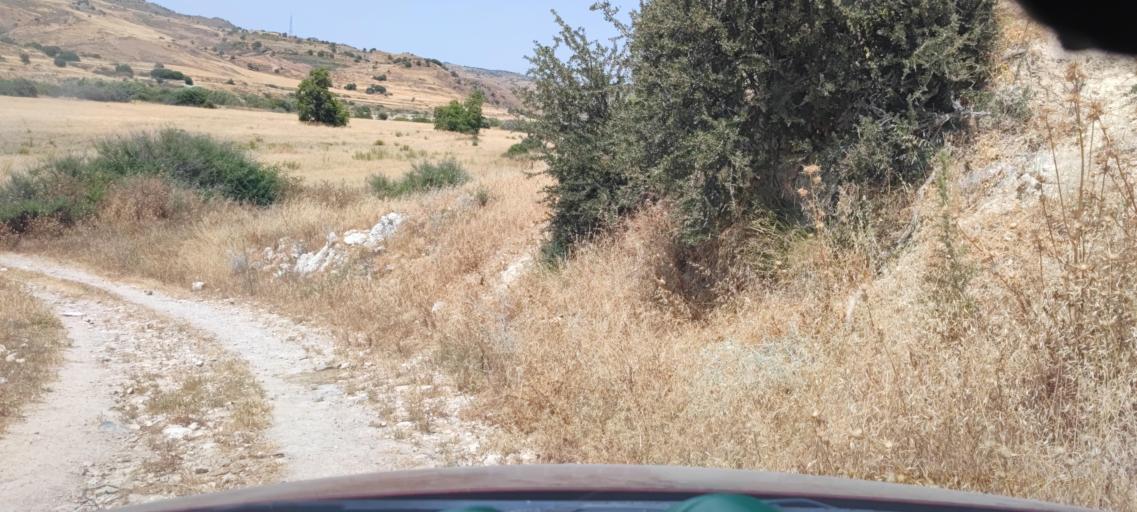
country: CY
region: Limassol
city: Pissouri
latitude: 34.7342
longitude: 32.6026
